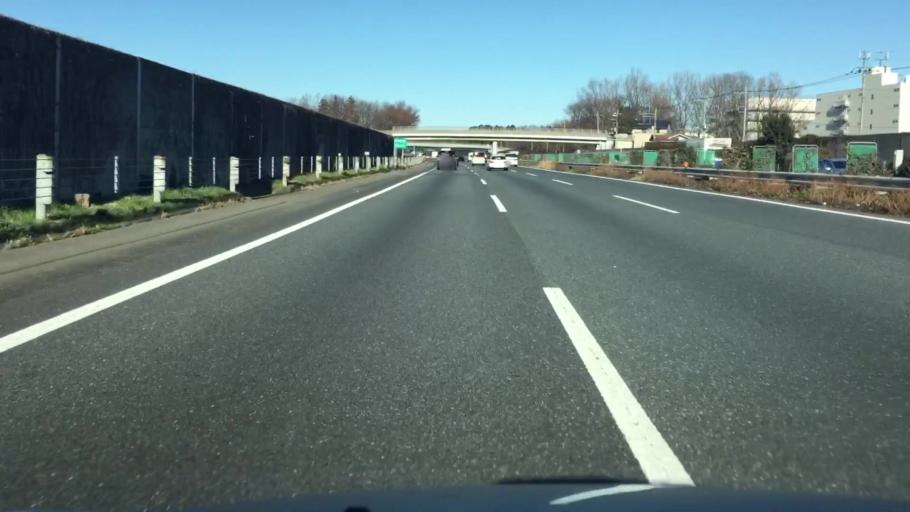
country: JP
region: Saitama
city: Ogawa
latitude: 36.1020
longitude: 139.2801
